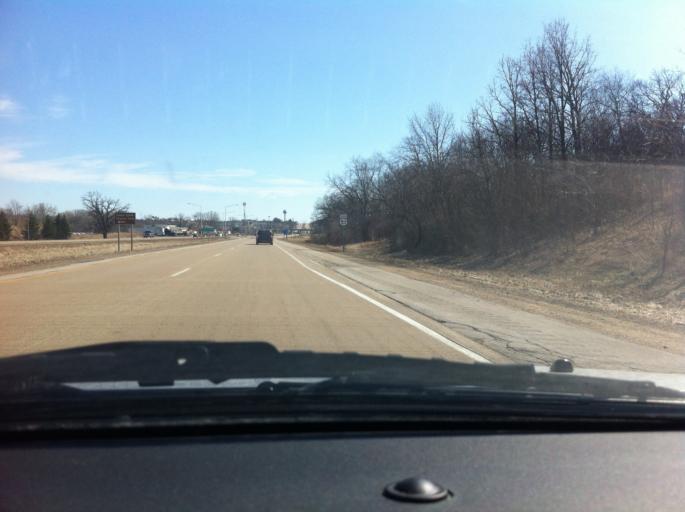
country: US
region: Wisconsin
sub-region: Dane County
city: Windsor
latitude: 43.1893
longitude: -89.3245
